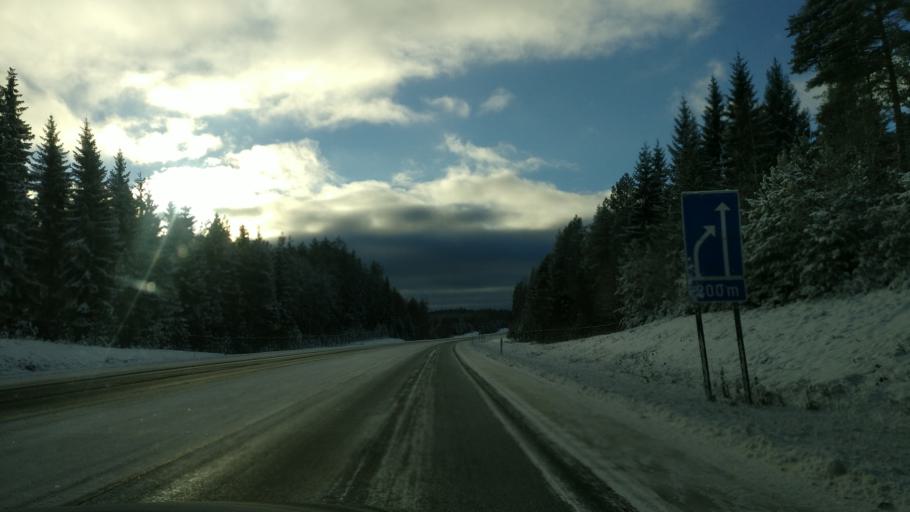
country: FI
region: Southern Savonia
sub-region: Mikkeli
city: Pertunmaa
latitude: 61.4096
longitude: 26.4098
